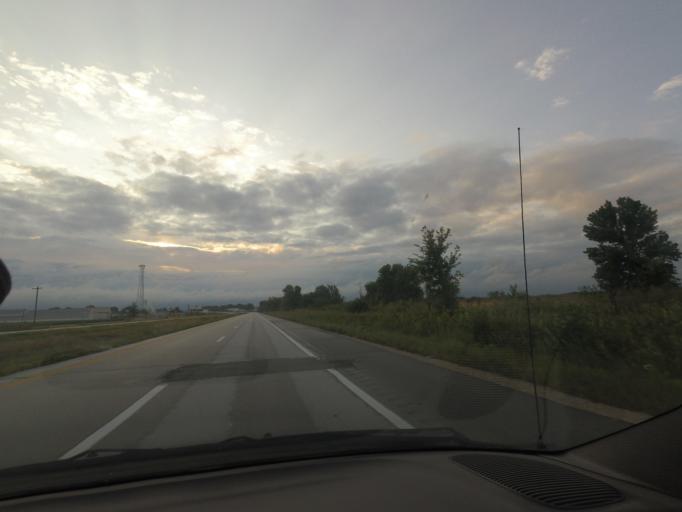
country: US
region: Missouri
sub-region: Shelby County
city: Shelbina
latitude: 39.6995
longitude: -92.0648
